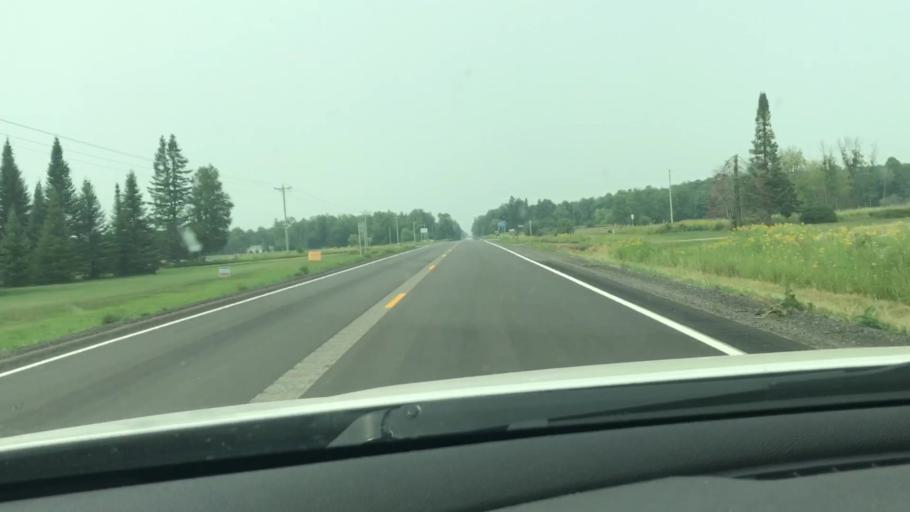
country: US
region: Minnesota
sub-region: Itasca County
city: Cohasset
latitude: 47.3544
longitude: -93.8477
